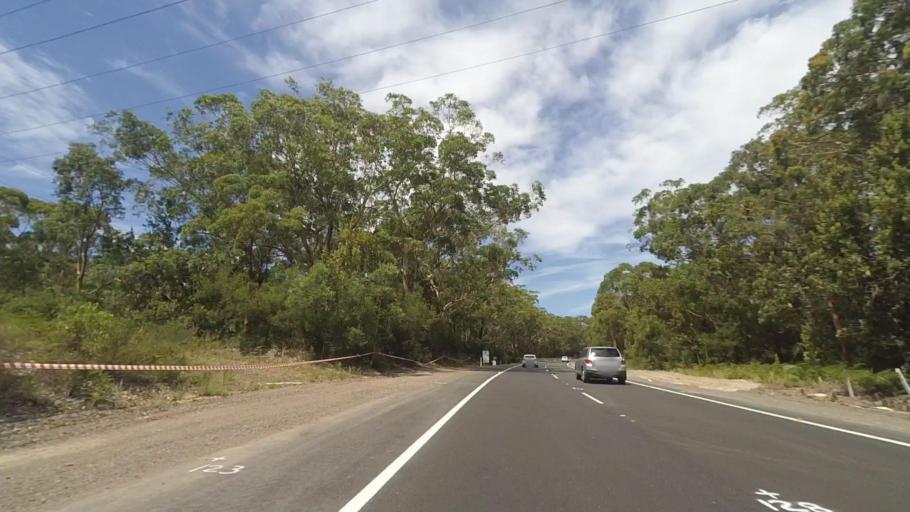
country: AU
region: New South Wales
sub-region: Port Stephens Shire
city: Anna Bay
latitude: -32.7797
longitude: 151.9889
